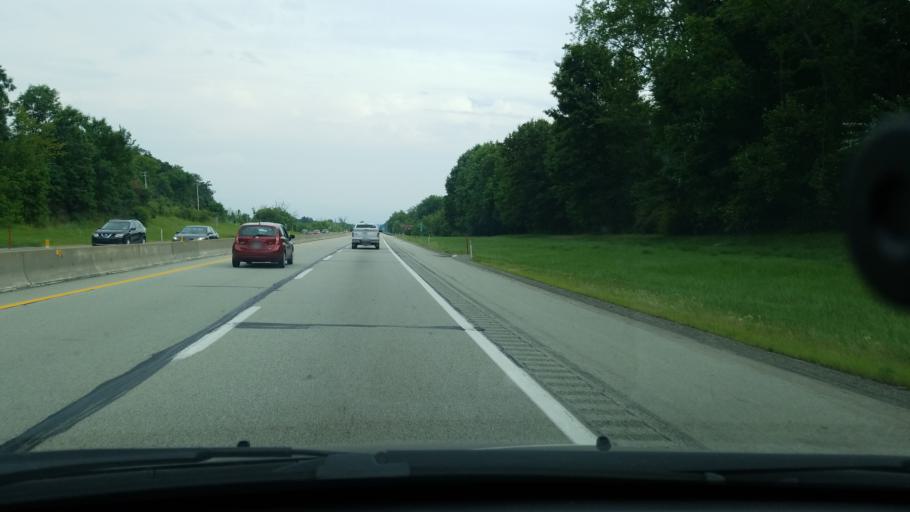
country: US
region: Pennsylvania
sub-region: Butler County
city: Fernway
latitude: 40.7036
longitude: -80.1215
